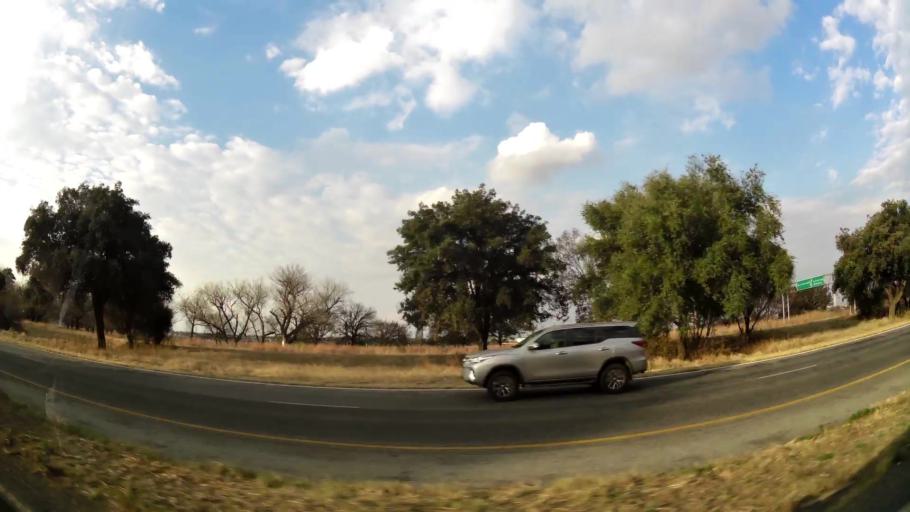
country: ZA
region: Orange Free State
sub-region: Fezile Dabi District Municipality
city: Sasolburg
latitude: -26.7978
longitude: 27.8308
